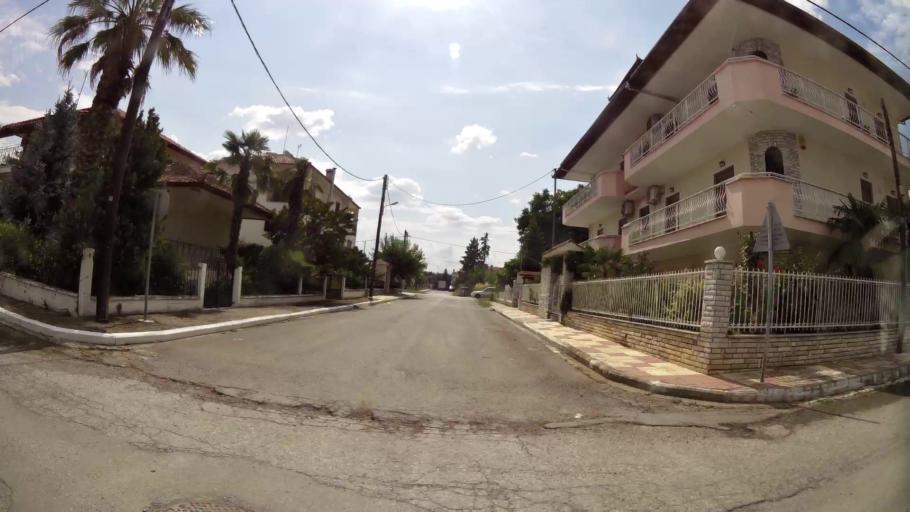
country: GR
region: Central Macedonia
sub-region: Nomos Pierias
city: Makrygialos
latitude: 40.4137
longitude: 22.6042
